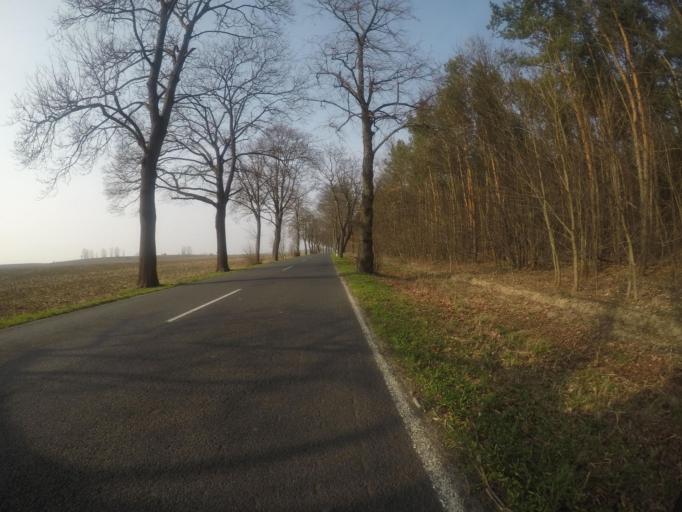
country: DE
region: Brandenburg
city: Schonefeld
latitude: 52.3415
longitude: 13.4884
